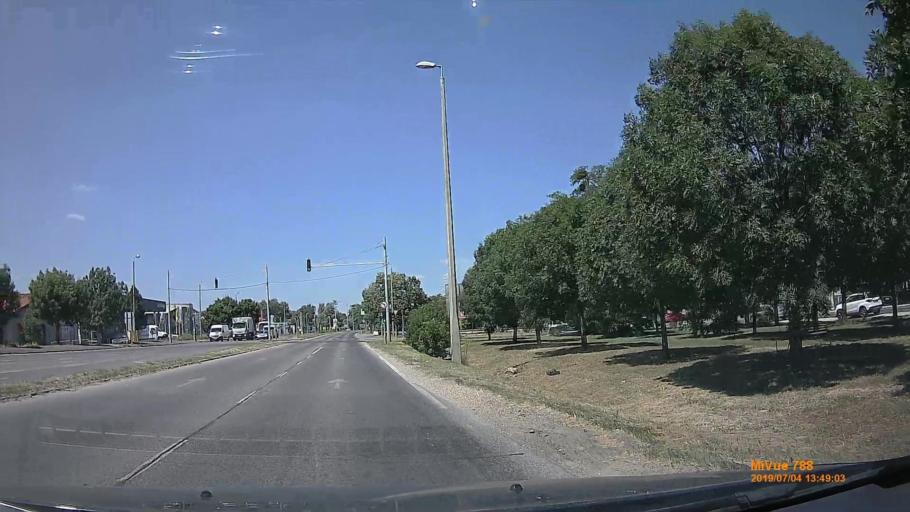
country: HU
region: Komarom-Esztergom
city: Tatabanya
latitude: 47.5940
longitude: 18.3892
